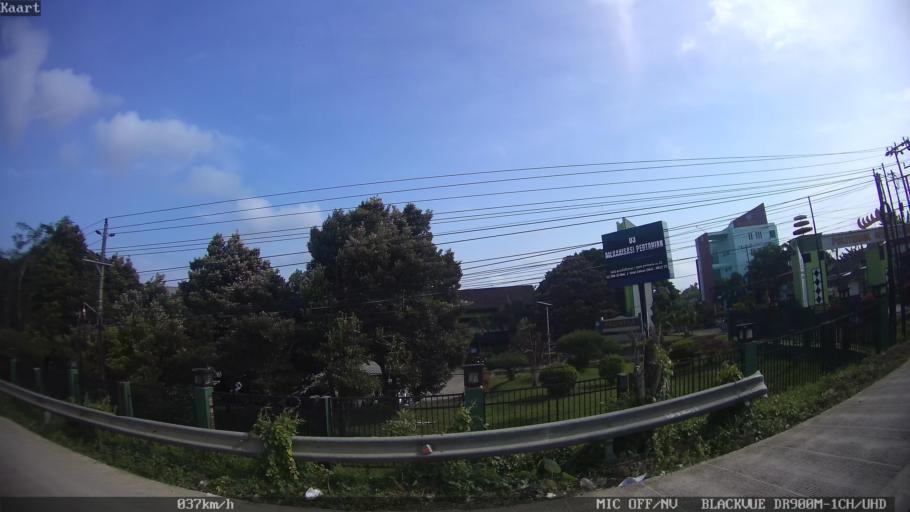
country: ID
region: Lampung
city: Kedaton
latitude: -5.3593
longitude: 105.2330
